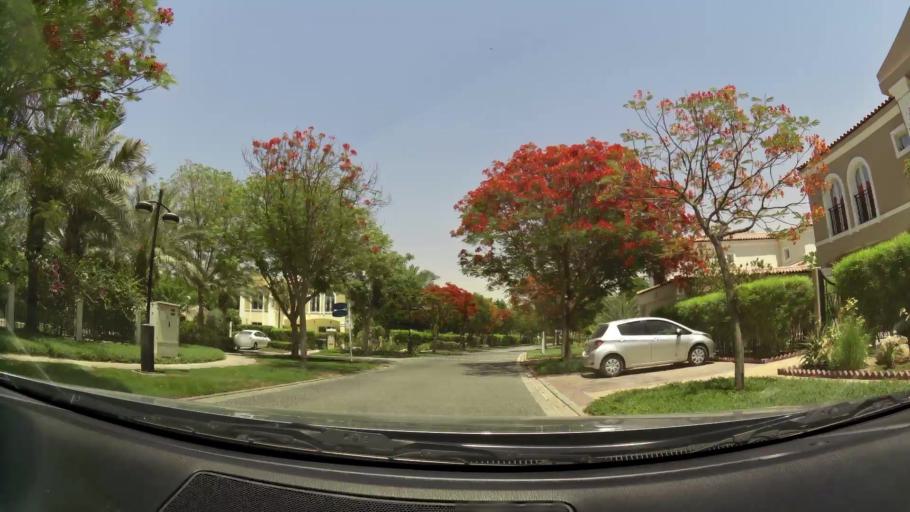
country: AE
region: Dubai
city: Dubai
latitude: 25.0005
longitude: 55.1627
